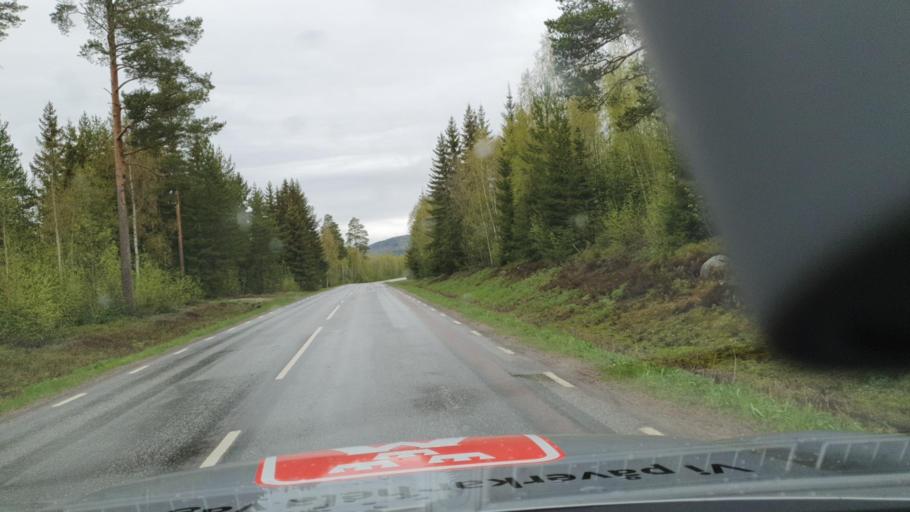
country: SE
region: Vaesternorrland
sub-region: OErnskoeldsviks Kommun
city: Bjasta
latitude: 63.3375
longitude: 18.5394
